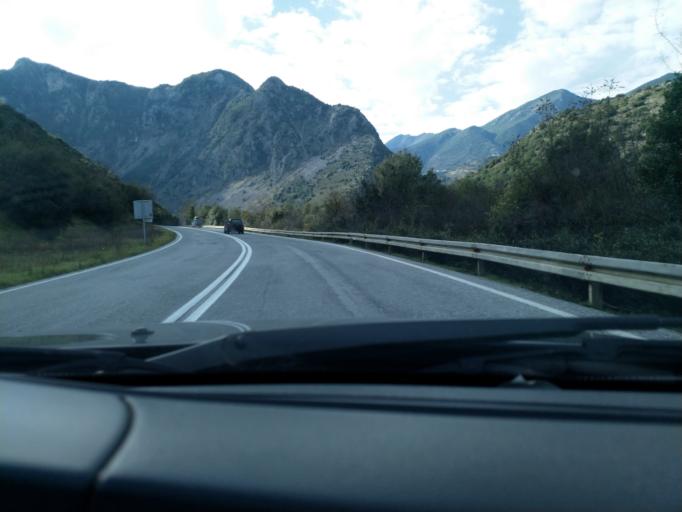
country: GR
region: Epirus
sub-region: Nomos Prevezis
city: Pappadates
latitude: 39.4073
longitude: 20.8368
